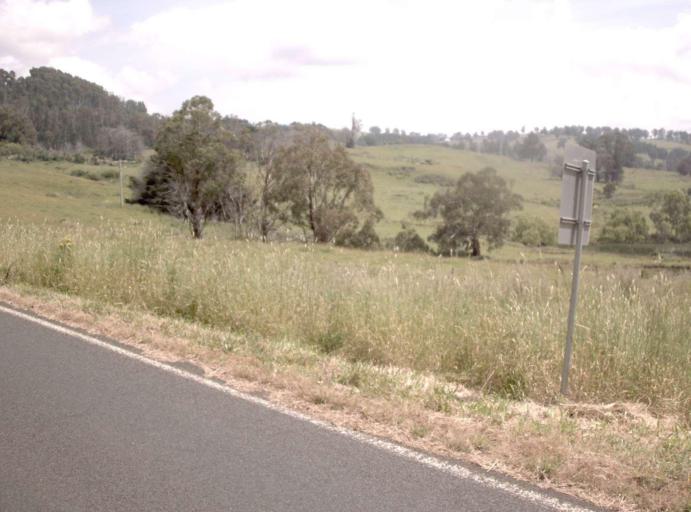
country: AU
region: Victoria
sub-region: Latrobe
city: Traralgon
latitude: -38.3359
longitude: 146.5723
